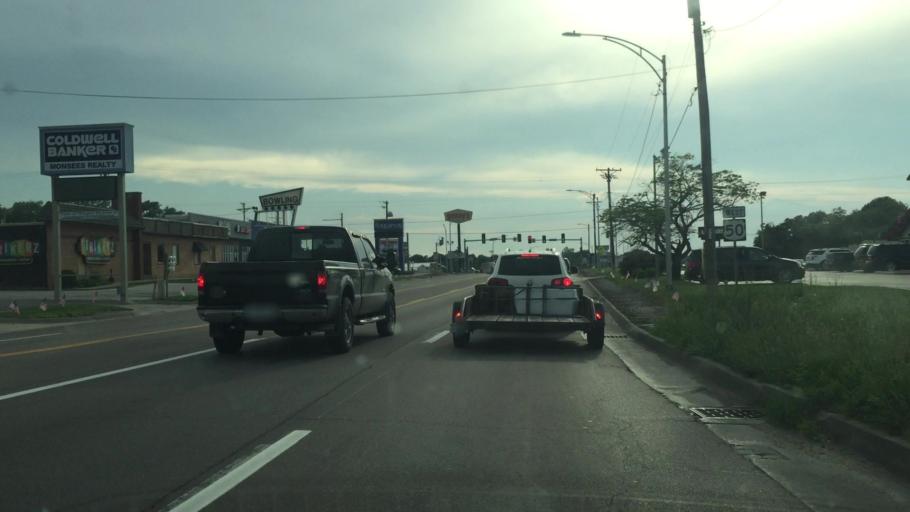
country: US
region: Missouri
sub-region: Pettis County
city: Sedalia
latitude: 38.7052
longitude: -93.2527
